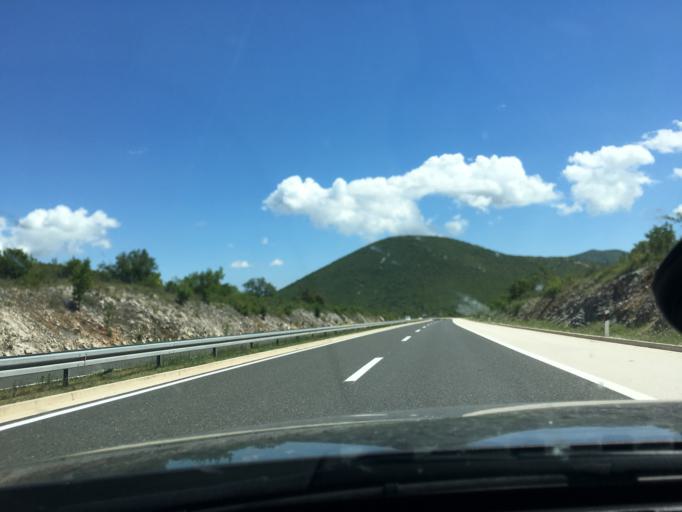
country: HR
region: Splitsko-Dalmatinska
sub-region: Grad Trogir
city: Trogir
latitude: 43.6400
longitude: 16.2079
